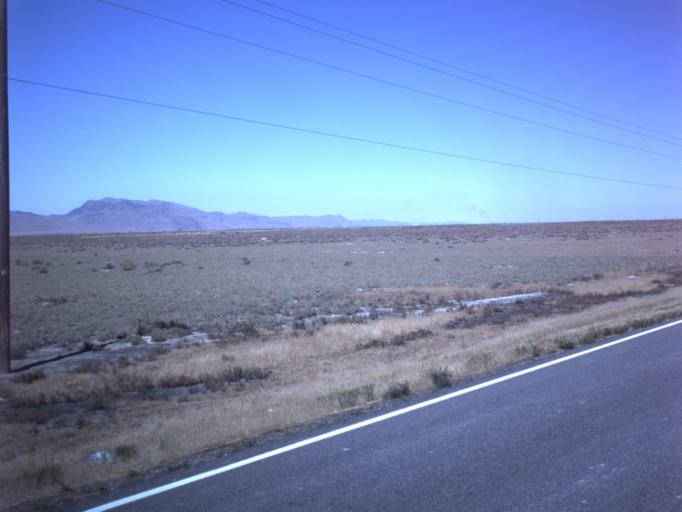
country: US
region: Utah
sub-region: Tooele County
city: Grantsville
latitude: 40.7196
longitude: -112.6605
